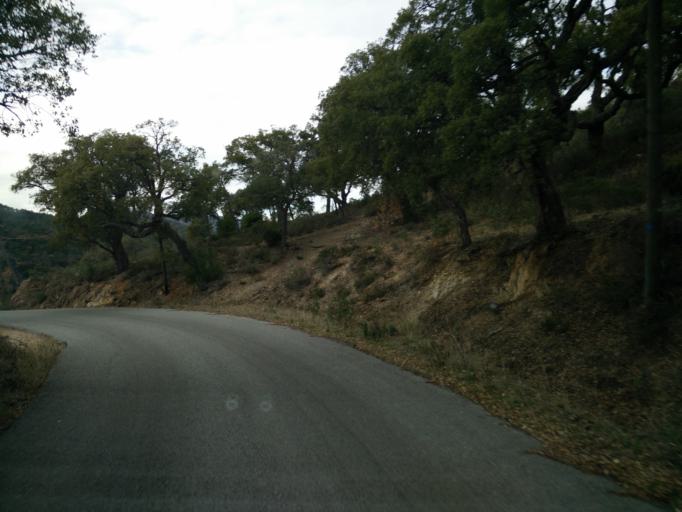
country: FR
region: Provence-Alpes-Cote d'Azur
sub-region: Departement du Var
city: Le Plan-de-la-Tour
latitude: 43.3679
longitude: 6.5999
